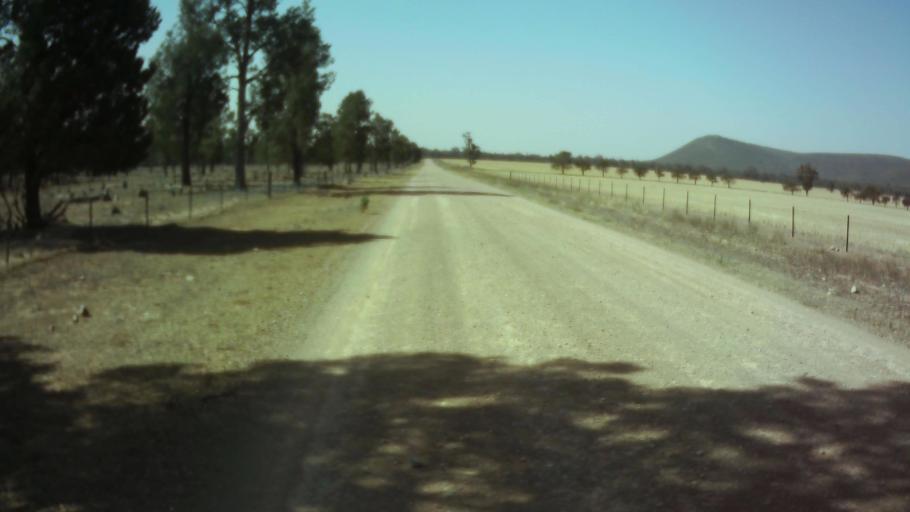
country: AU
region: New South Wales
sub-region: Weddin
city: Grenfell
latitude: -33.9321
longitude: 147.9306
